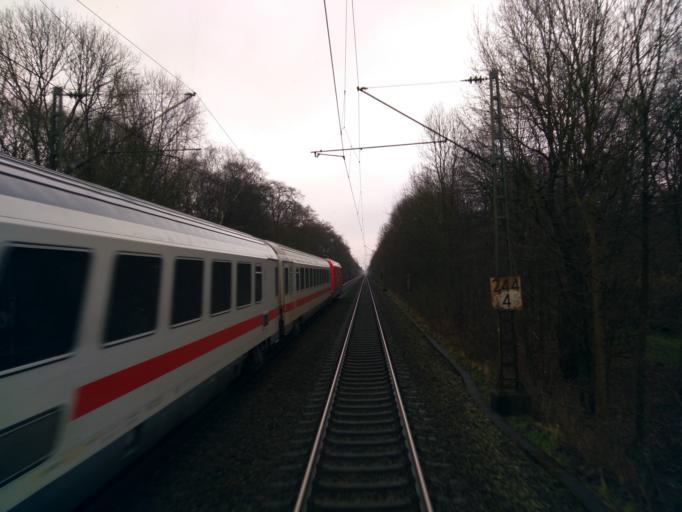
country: DE
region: Bremen
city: Bremen
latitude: 53.1025
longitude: 8.8295
